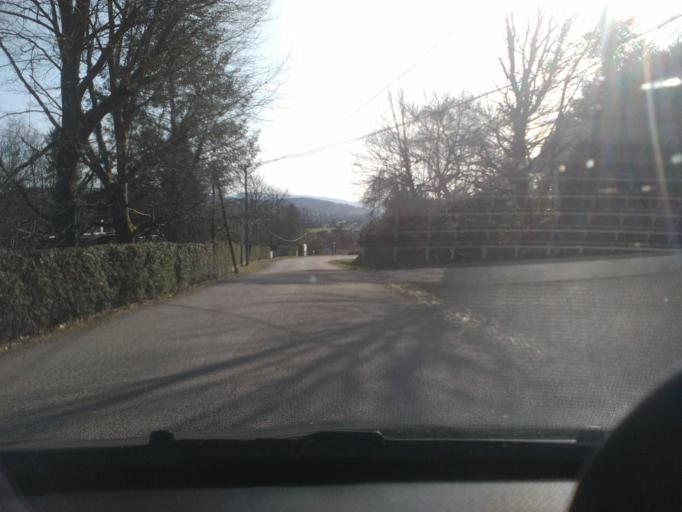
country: FR
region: Lorraine
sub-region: Departement des Vosges
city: Sainte-Marguerite
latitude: 48.2801
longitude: 6.9857
